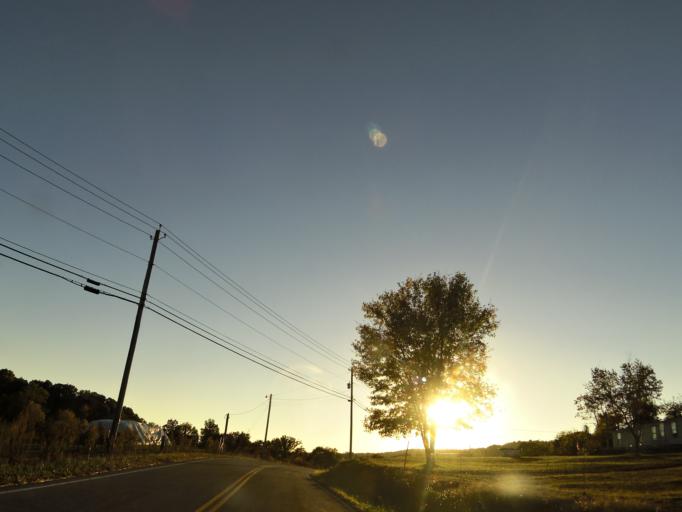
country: US
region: Tennessee
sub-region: Grainger County
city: Rutledge
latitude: 36.2754
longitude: -83.6298
